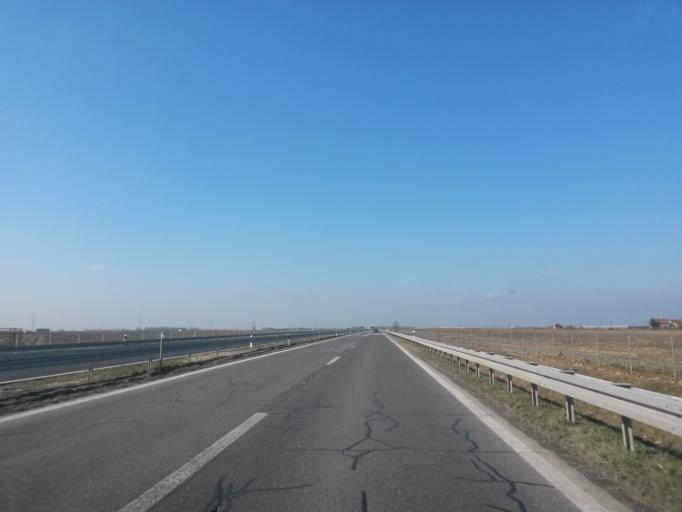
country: HR
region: Osjecko-Baranjska
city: Josipovac
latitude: 45.5673
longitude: 18.5862
